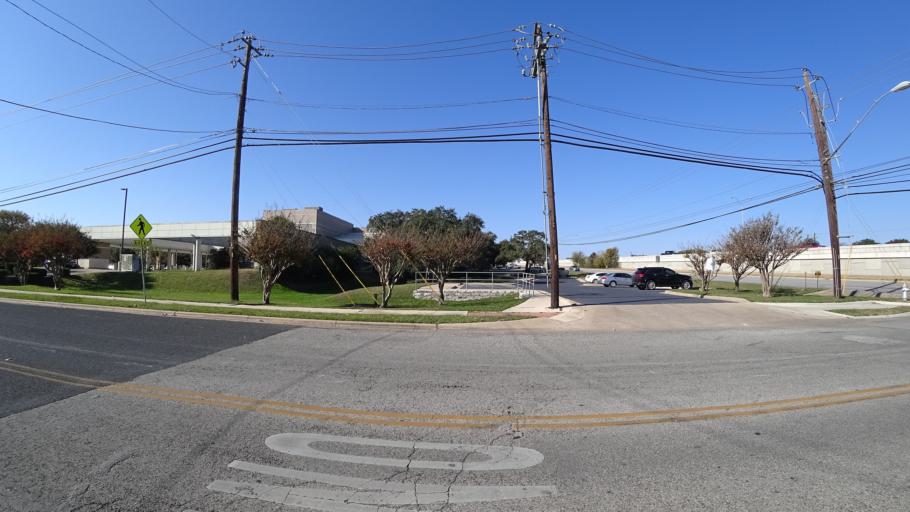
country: US
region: Texas
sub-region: Travis County
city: Barton Creek
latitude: 30.2357
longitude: -97.8460
